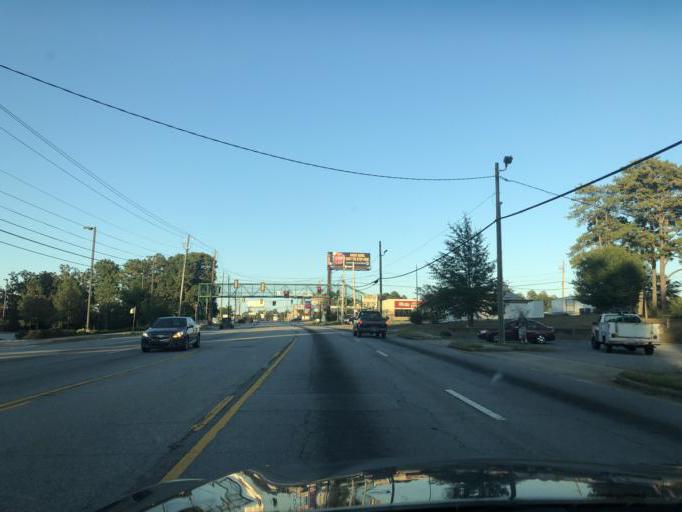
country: US
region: Georgia
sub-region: Muscogee County
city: Columbus
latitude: 32.4657
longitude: -84.9177
